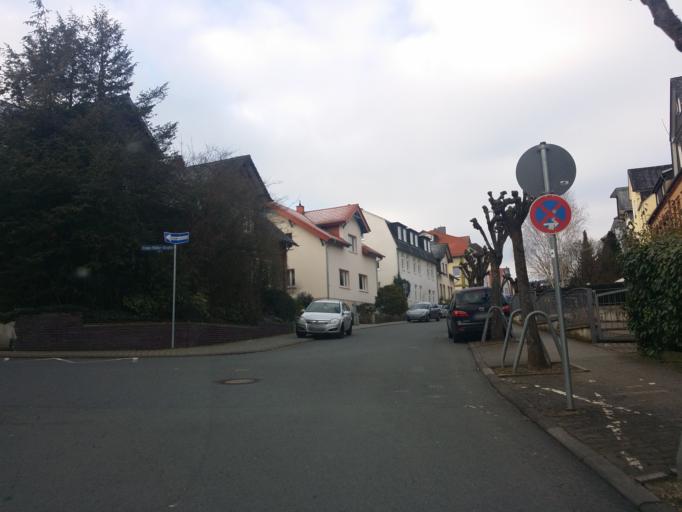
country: DE
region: Hesse
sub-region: Regierungsbezirk Darmstadt
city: Idstein
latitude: 50.2187
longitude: 8.2638
